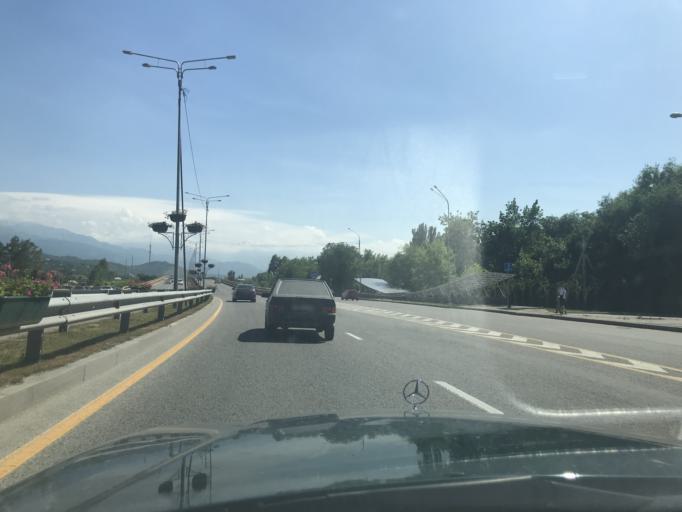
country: KZ
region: Almaty Qalasy
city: Almaty
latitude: 43.2875
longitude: 76.9879
